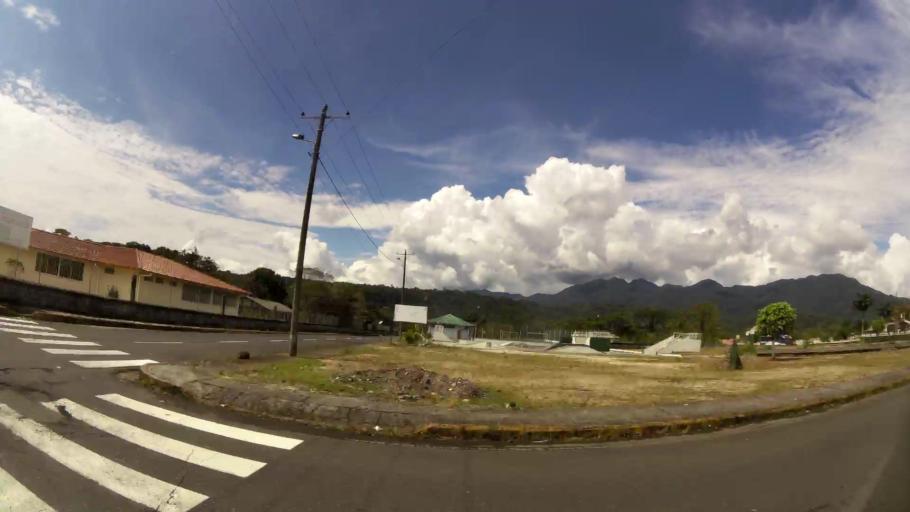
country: EC
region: Pastaza
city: Puyo
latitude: -1.4639
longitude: -78.1088
